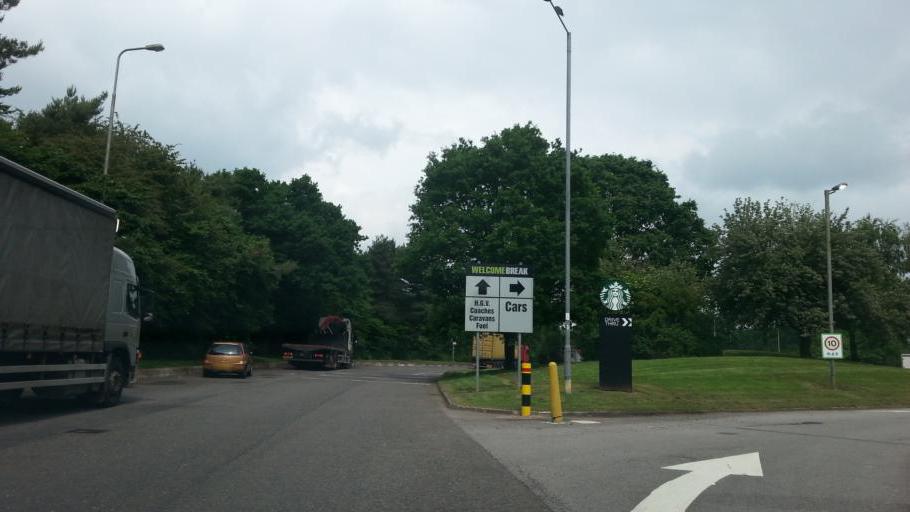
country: GB
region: England
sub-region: Coventry
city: Keresley
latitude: 52.4723
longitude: -1.5499
